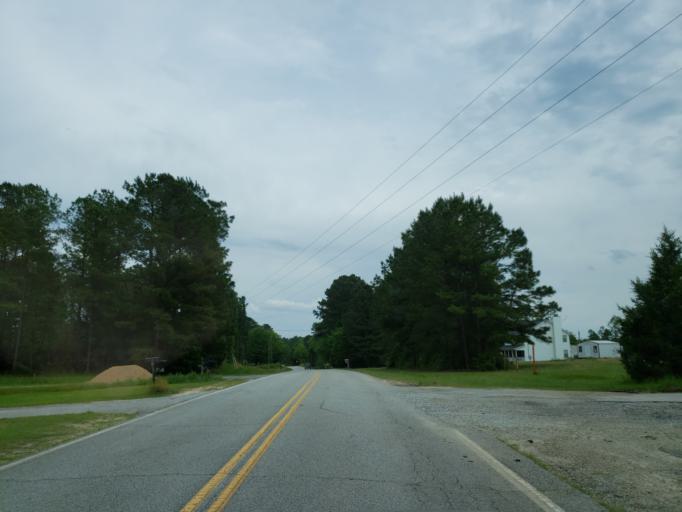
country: US
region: Georgia
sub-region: Bibb County
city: West Point
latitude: 32.8216
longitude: -83.8678
